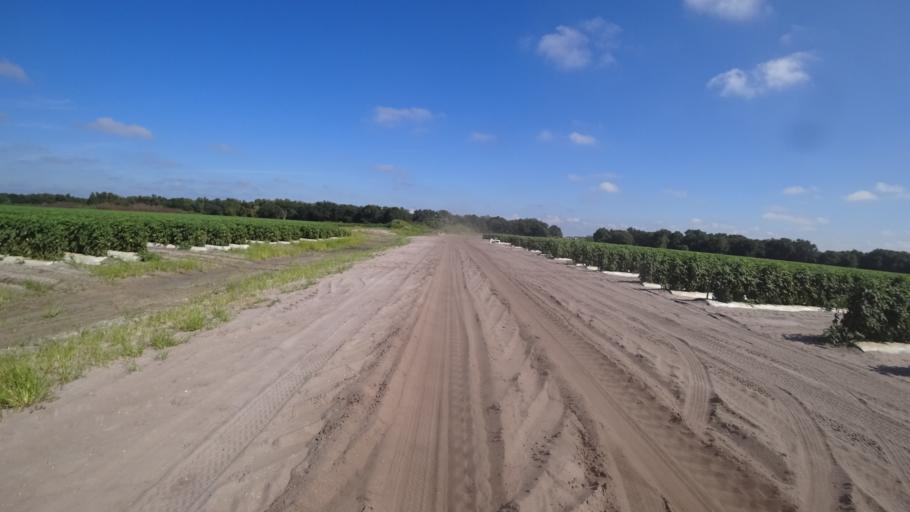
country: US
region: Florida
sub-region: DeSoto County
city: Arcadia
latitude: 27.2947
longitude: -82.0465
